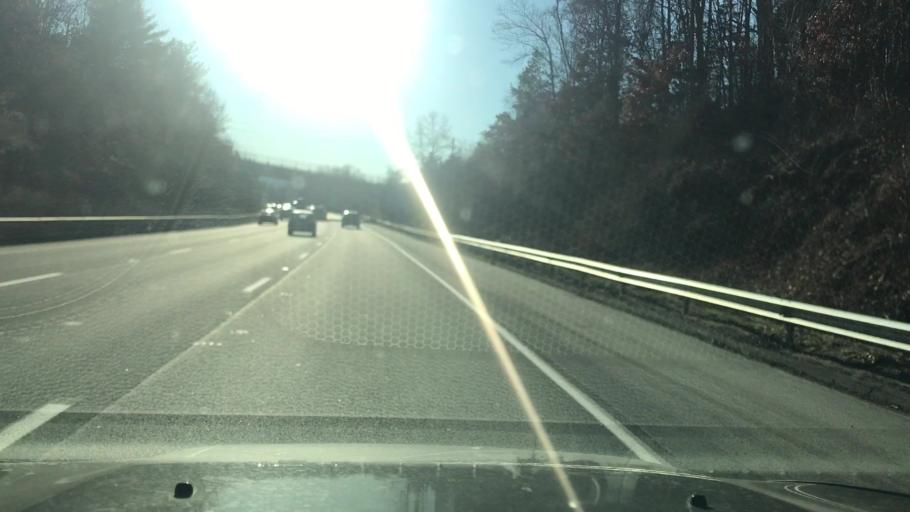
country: US
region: Connecticut
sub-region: Hartford County
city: Plainville
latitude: 41.6204
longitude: -72.8927
